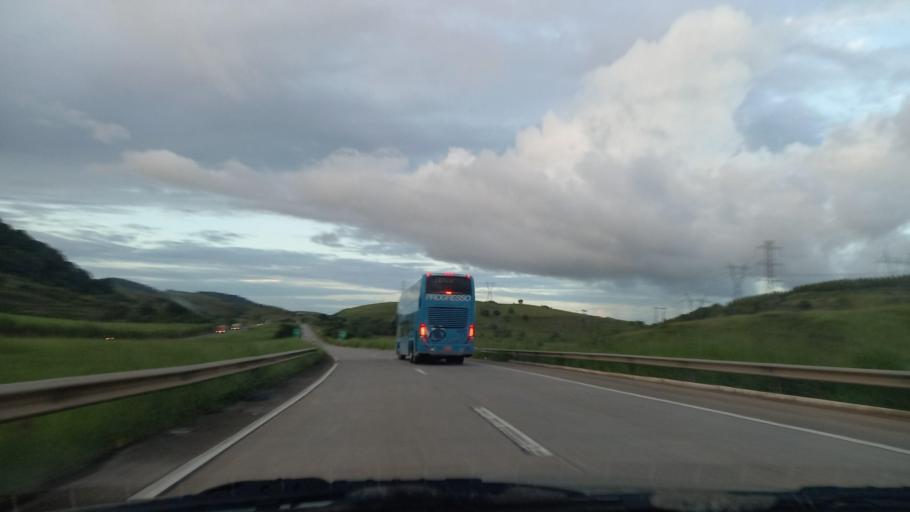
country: BR
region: Pernambuco
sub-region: Joaquim Nabuco
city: Joaquim Nabuco
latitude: -8.6028
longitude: -35.5318
